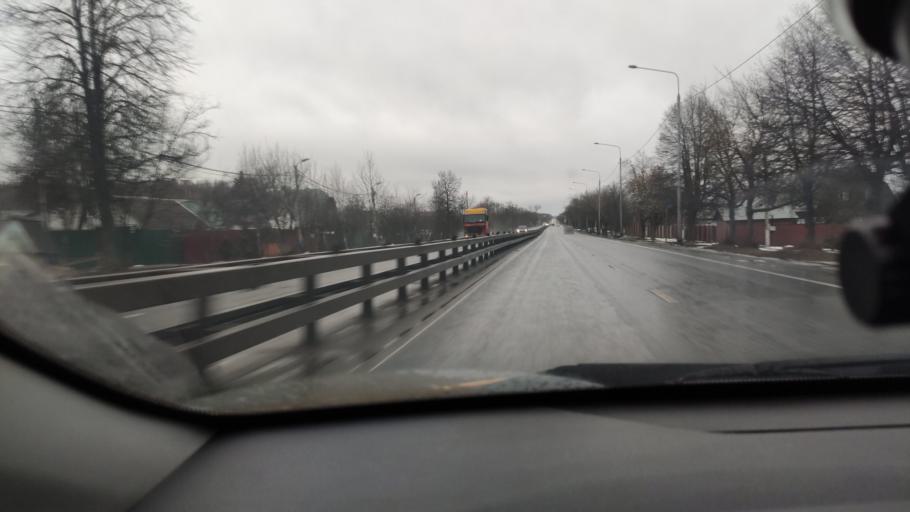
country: RU
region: Moskovskaya
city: Troitsk
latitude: 55.3277
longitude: 37.2750
